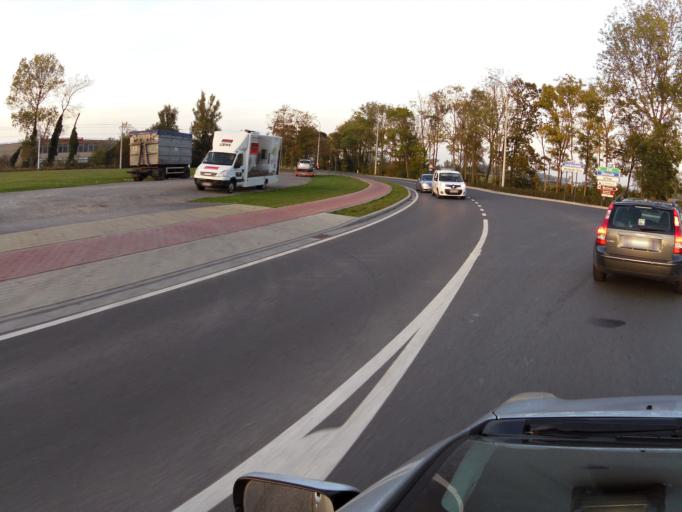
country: BE
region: Flanders
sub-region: Provincie West-Vlaanderen
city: Nieuwpoort
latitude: 51.1373
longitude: 2.7550
